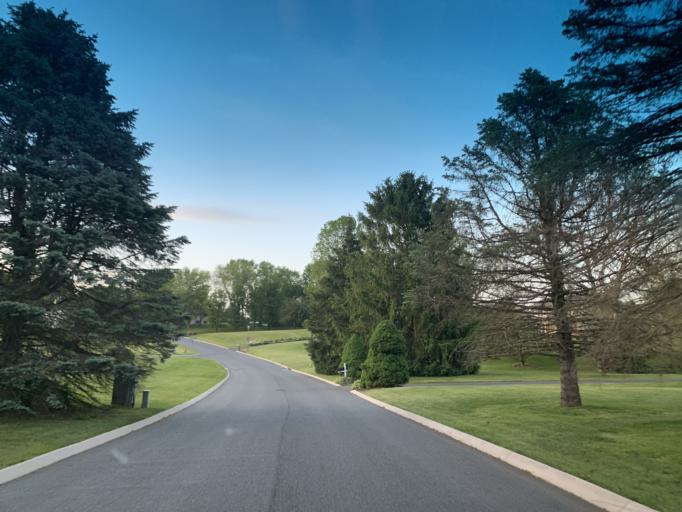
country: US
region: Maryland
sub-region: Harford County
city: South Bel Air
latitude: 39.5873
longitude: -76.2778
